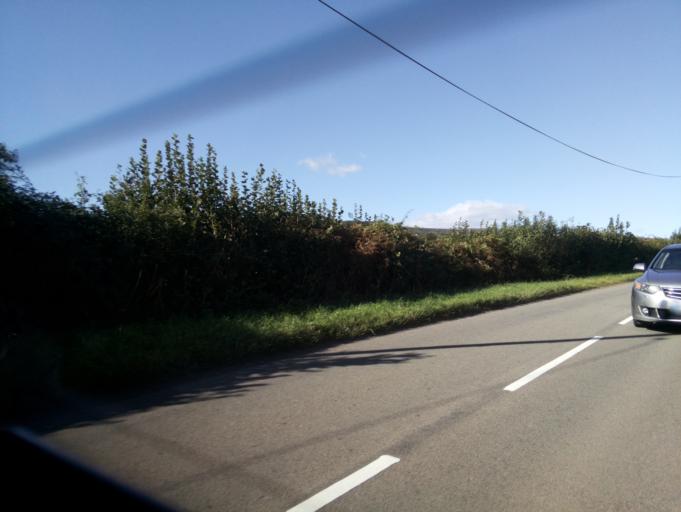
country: GB
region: Wales
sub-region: Torfaen County Borough
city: Cwmbran
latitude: 51.6247
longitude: -3.0517
